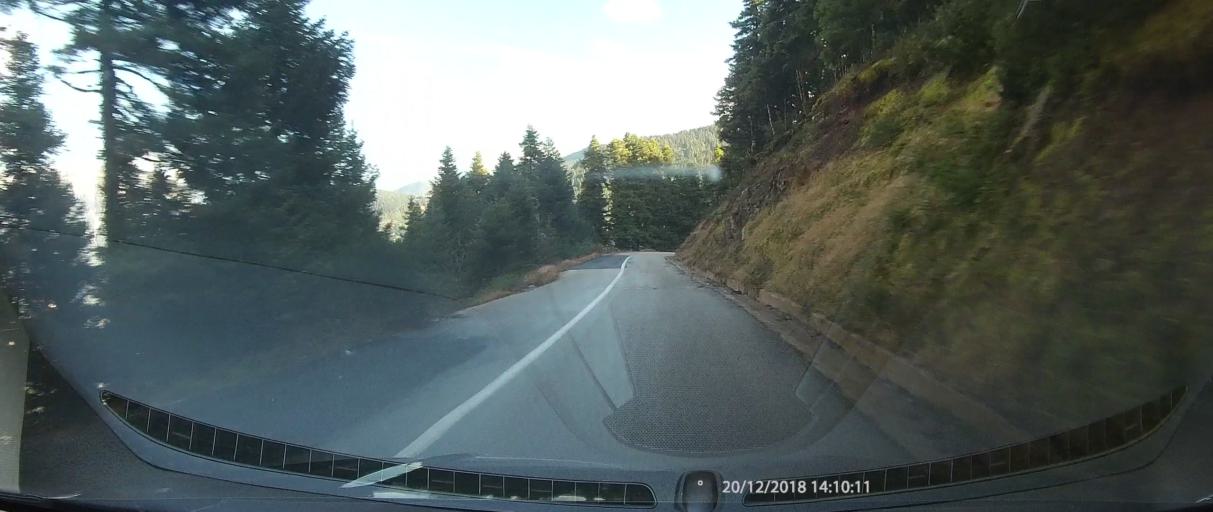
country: GR
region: West Greece
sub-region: Nomos Aitolias kai Akarnanias
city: Thermo
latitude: 38.7472
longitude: 21.6481
